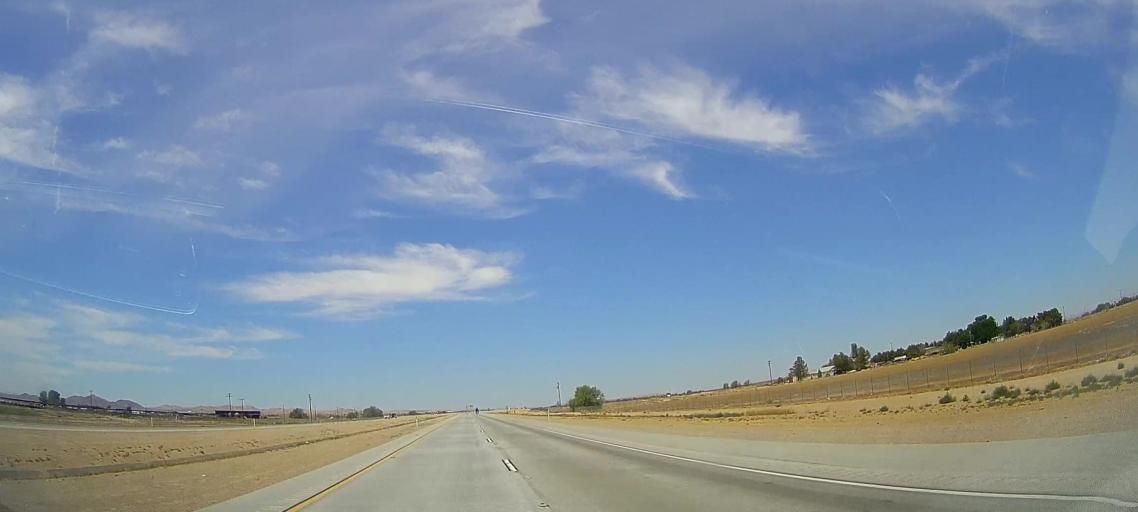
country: US
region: California
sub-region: San Bernardino County
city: Lenwood
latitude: 34.9156
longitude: -117.1338
